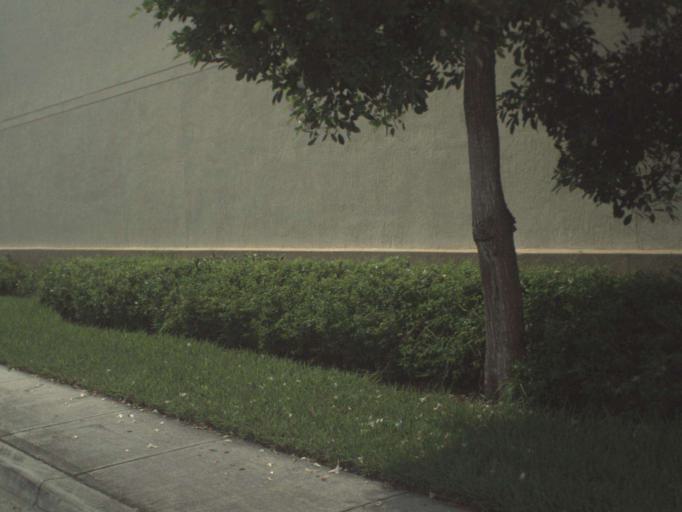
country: US
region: Florida
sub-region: Miami-Dade County
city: Coral Gables
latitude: 25.7337
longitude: -80.2530
